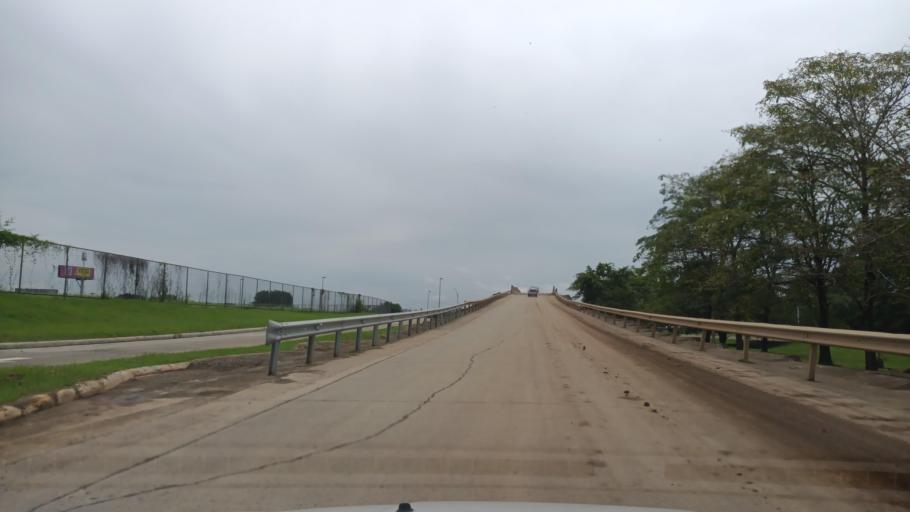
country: PA
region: Panama
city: Tocumen
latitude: 9.0388
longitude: -79.4050
